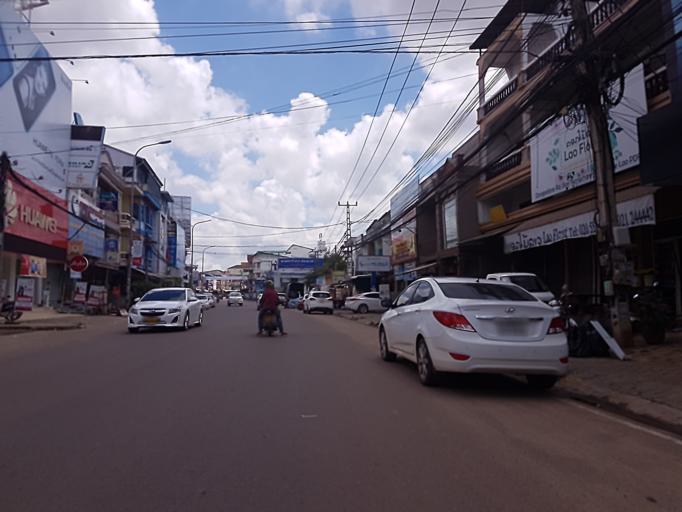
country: LA
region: Vientiane
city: Vientiane
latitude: 17.9644
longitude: 102.6193
